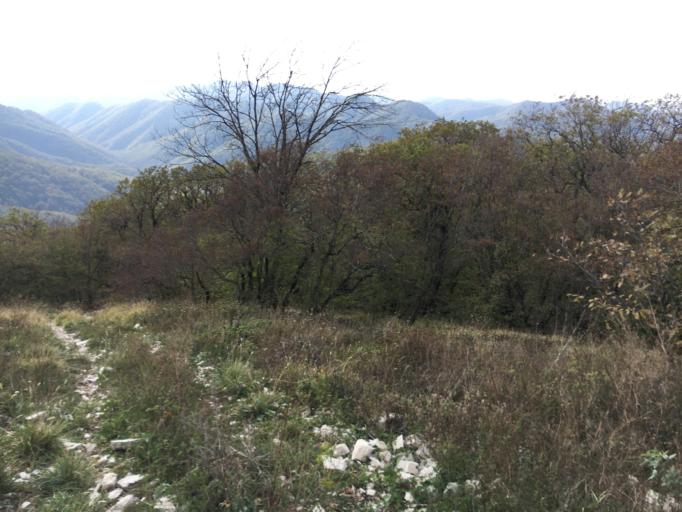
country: RU
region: Krasnodarskiy
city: Nebug
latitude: 44.2413
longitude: 38.9861
